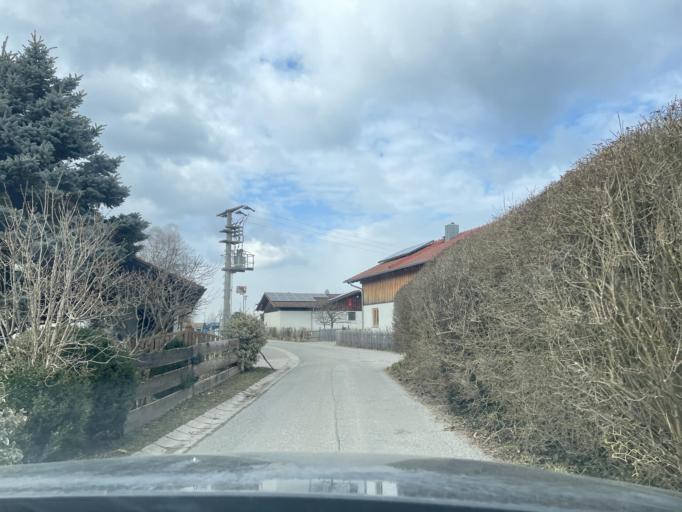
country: DE
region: Bavaria
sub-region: Lower Bavaria
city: Viechtach
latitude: 49.0785
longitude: 12.9081
